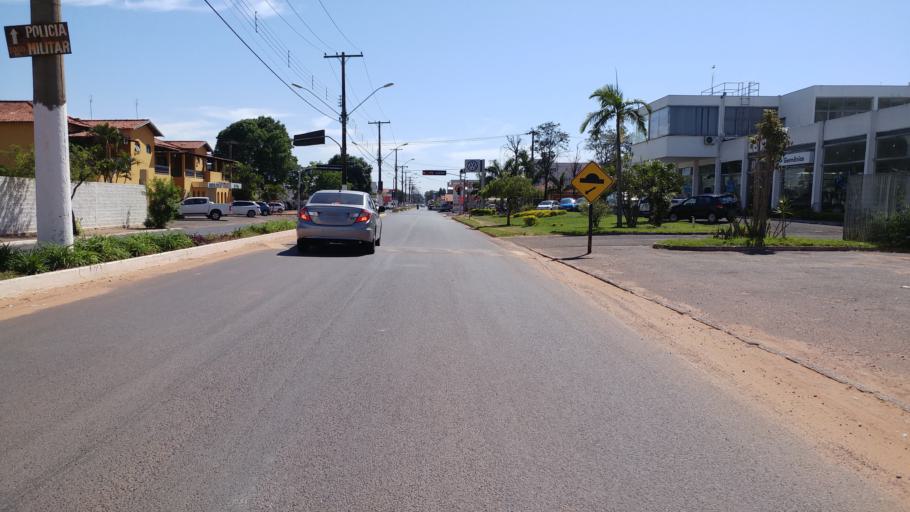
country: BR
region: Sao Paulo
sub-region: Paraguacu Paulista
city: Paraguacu Paulista
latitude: -22.4306
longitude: -50.5858
